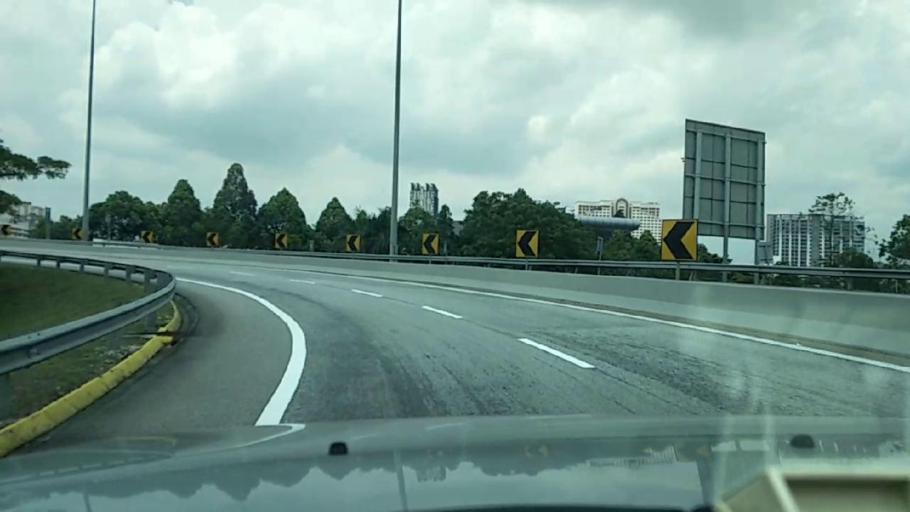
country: MY
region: Kuala Lumpur
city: Kuala Lumpur
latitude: 3.0916
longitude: 101.6703
